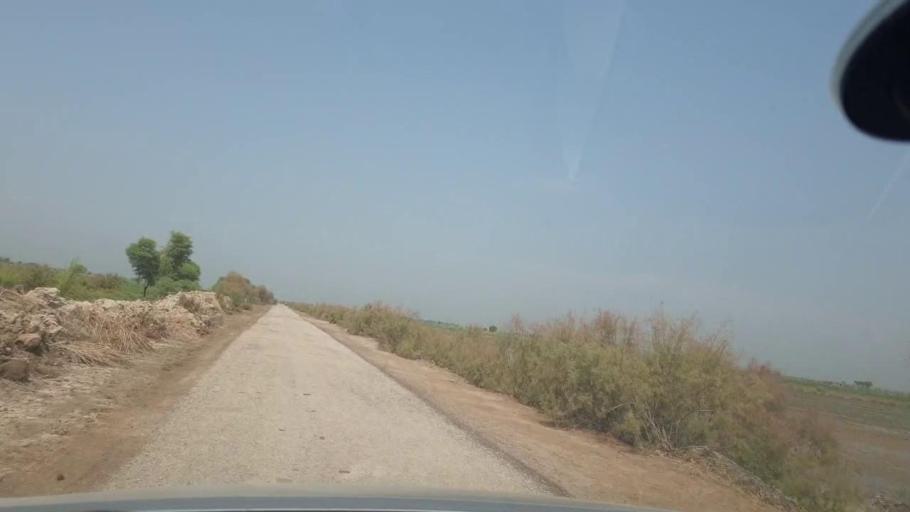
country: PK
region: Balochistan
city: Mehrabpur
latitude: 28.0588
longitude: 68.0727
